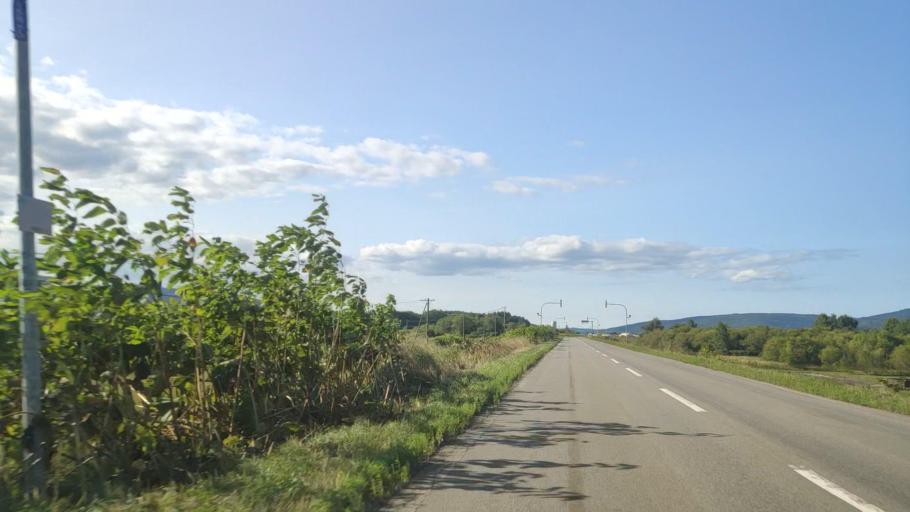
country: JP
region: Hokkaido
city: Nayoro
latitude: 44.8081
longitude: 142.0666
